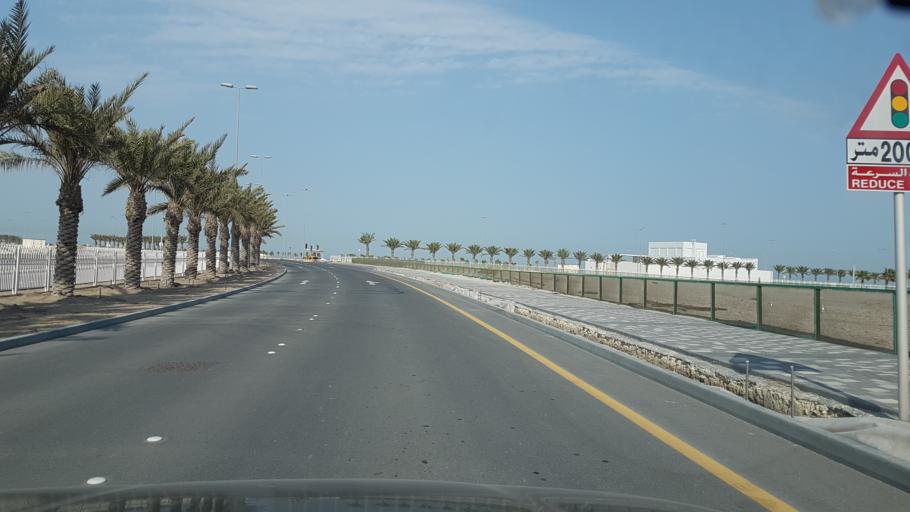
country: BH
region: Muharraq
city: Al Hadd
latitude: 26.2700
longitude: 50.6771
